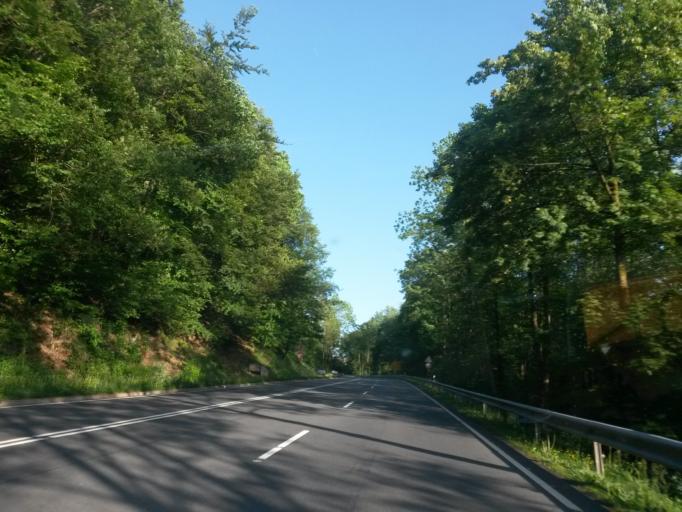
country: DE
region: North Rhine-Westphalia
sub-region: Regierungsbezirk Arnsberg
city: Drolshagen
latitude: 51.0475
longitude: 7.7354
